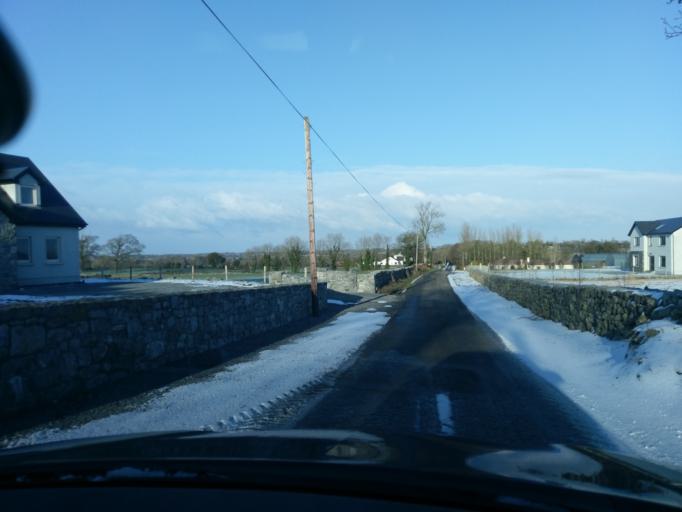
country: IE
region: Connaught
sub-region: County Galway
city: Athenry
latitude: 53.1759
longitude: -8.7406
